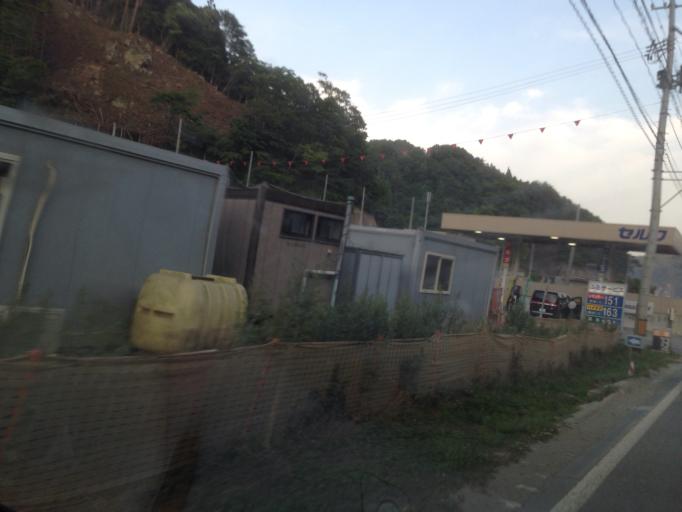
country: JP
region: Iwate
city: Kamaishi
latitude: 39.3097
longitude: 141.8890
